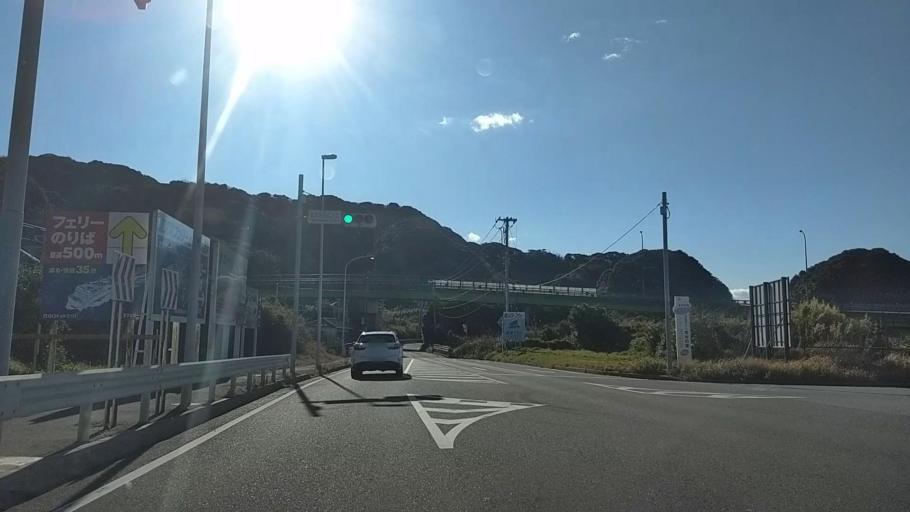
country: JP
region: Chiba
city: Futtsu
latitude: 35.1750
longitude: 139.8189
